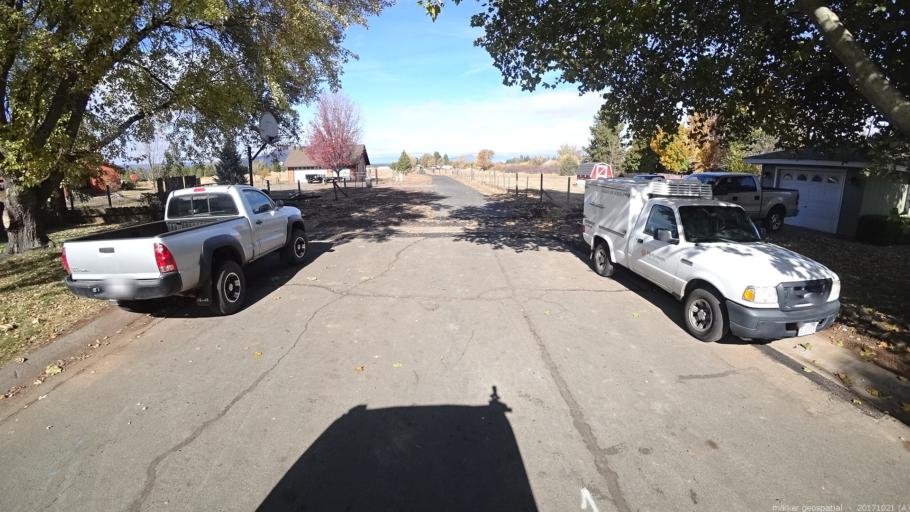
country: US
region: California
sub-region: Shasta County
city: Burney
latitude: 40.8874
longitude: -121.6604
